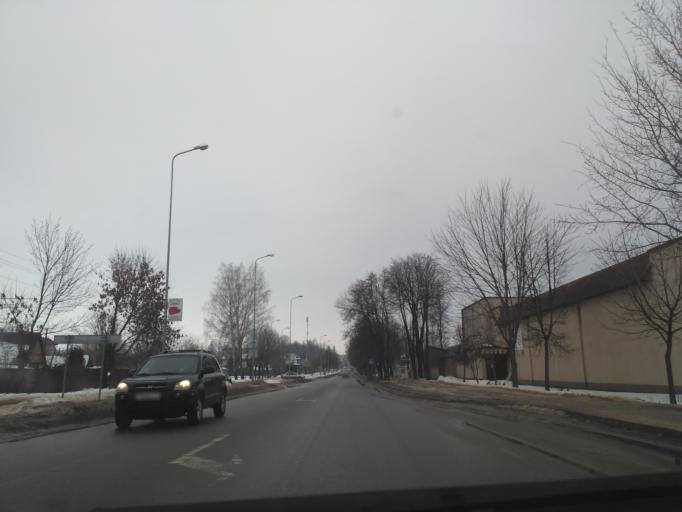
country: BY
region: Minsk
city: Horad Zhodzina
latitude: 54.0969
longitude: 28.3385
